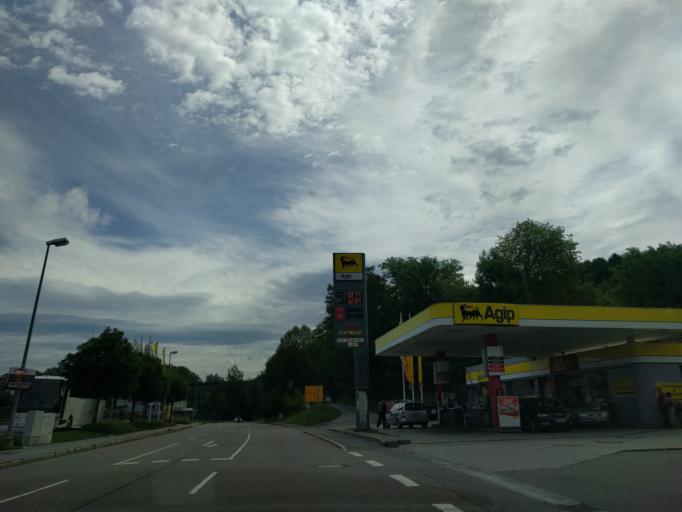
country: DE
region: Bavaria
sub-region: Lower Bavaria
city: Regen
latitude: 48.9720
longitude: 13.1373
